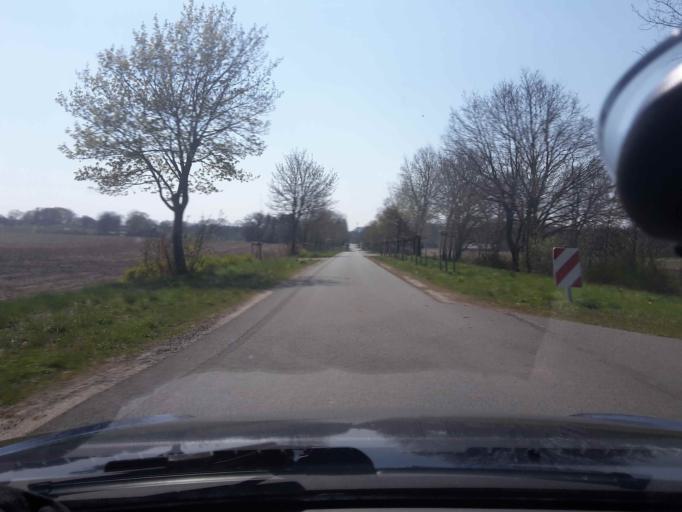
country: DE
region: Lower Saxony
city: Schneverdingen
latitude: 53.0867
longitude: 9.8611
